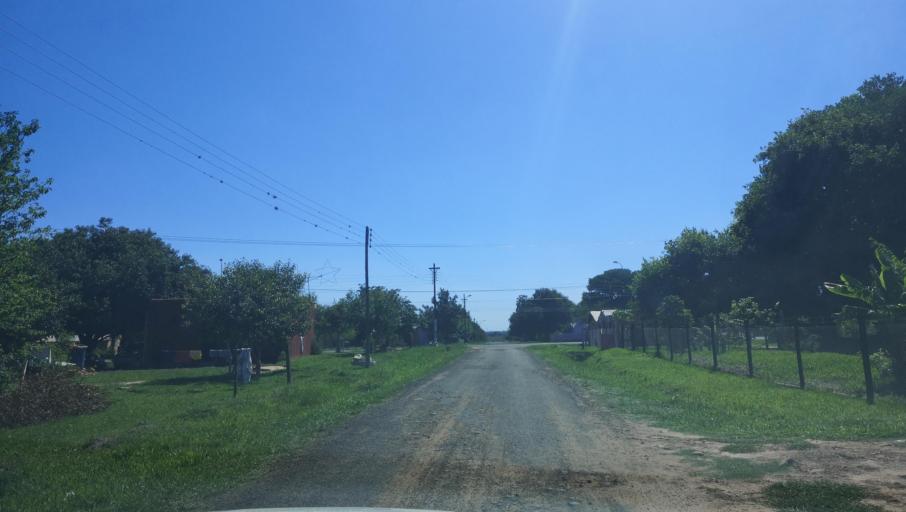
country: PY
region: Caaguazu
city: Carayao
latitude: -25.2052
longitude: -56.3983
